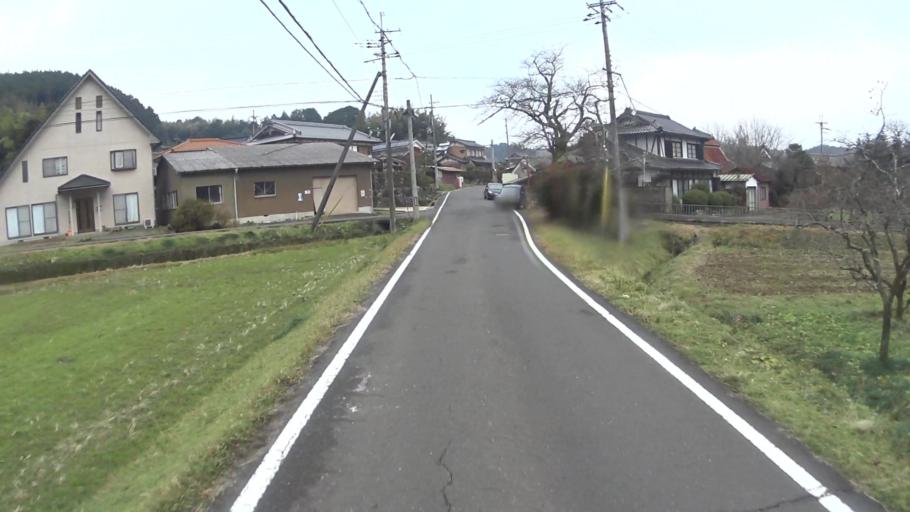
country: JP
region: Kyoto
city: Maizuru
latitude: 35.4282
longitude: 135.2963
